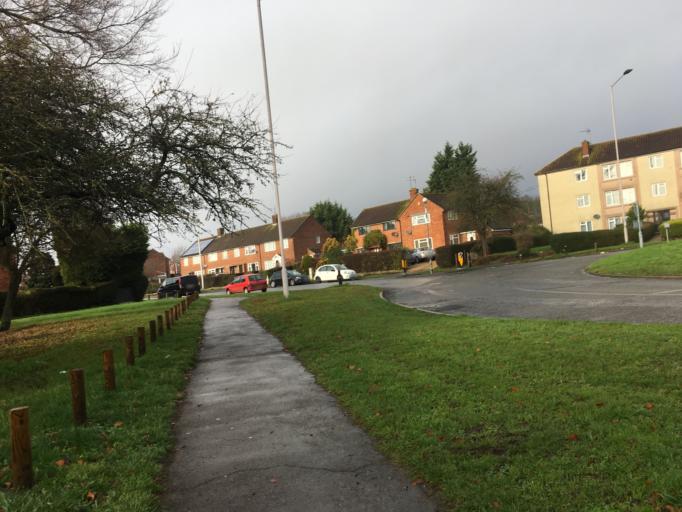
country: GB
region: England
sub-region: West Berkshire
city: Tilehurst
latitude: 51.4423
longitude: -1.0145
